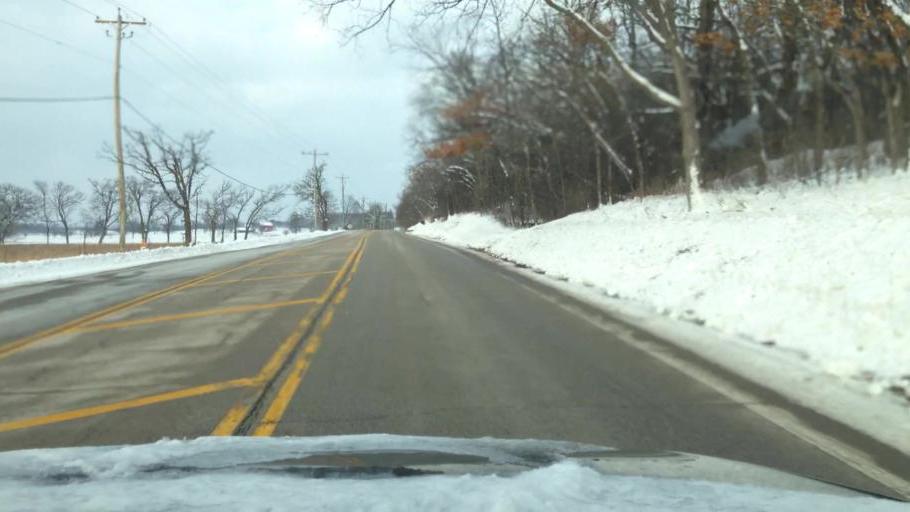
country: US
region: Wisconsin
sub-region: Waukesha County
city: North Prairie
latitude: 42.8906
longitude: -88.4170
